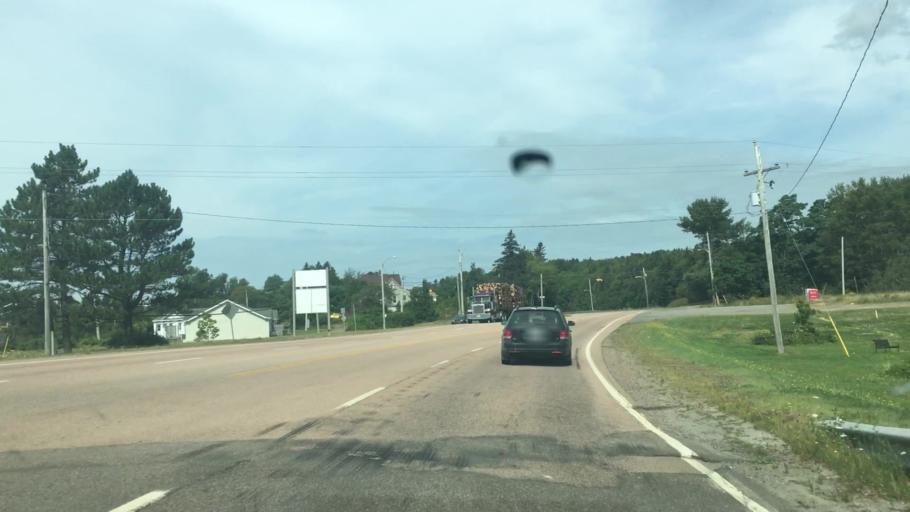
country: CA
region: Nova Scotia
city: Port Hawkesbury
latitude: 45.6225
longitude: -61.3645
